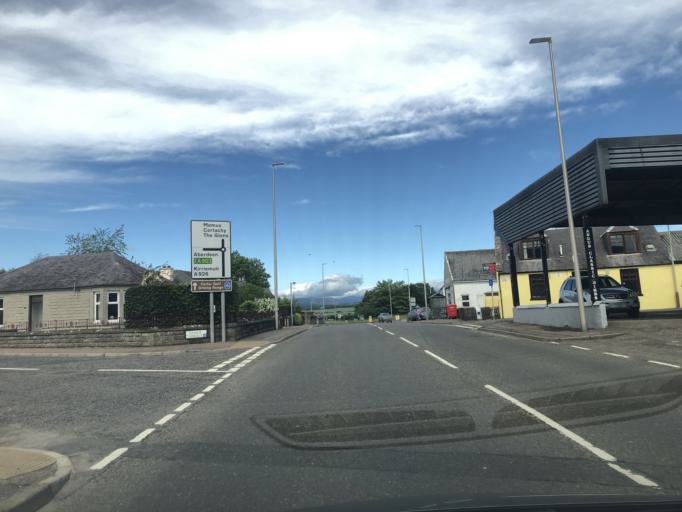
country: GB
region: Scotland
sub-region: Angus
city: Forfar
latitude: 56.6517
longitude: -2.8904
